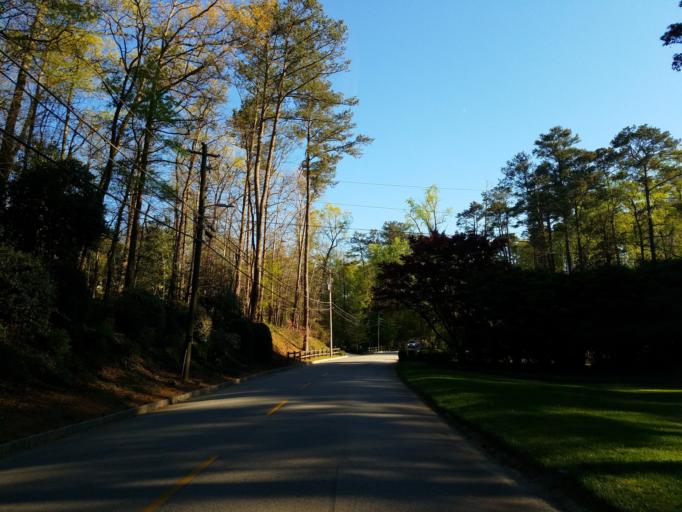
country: US
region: Georgia
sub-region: Cobb County
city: Vinings
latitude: 33.8425
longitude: -84.4406
